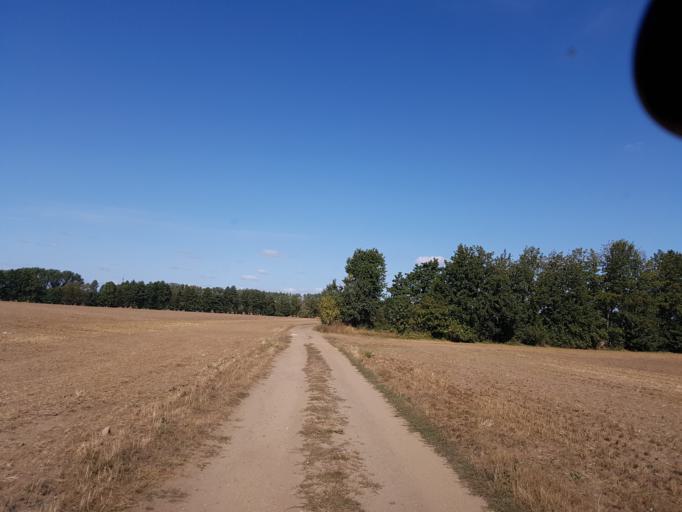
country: DE
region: Brandenburg
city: Luckau
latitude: 51.8431
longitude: 13.6362
